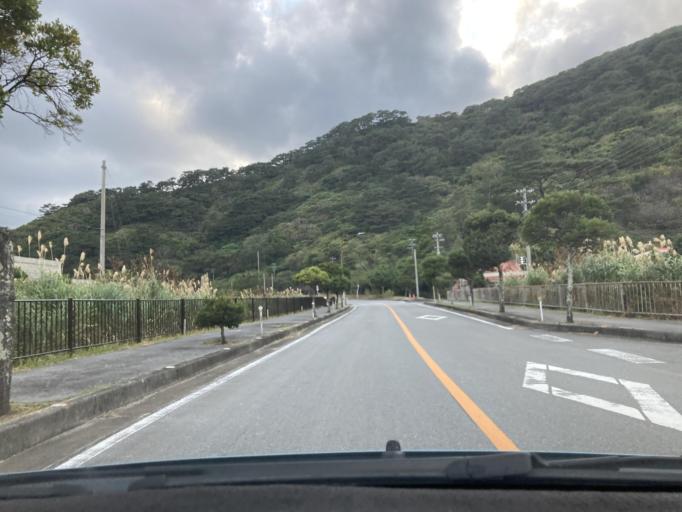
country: JP
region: Okinawa
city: Nago
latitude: 26.8372
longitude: 128.2876
